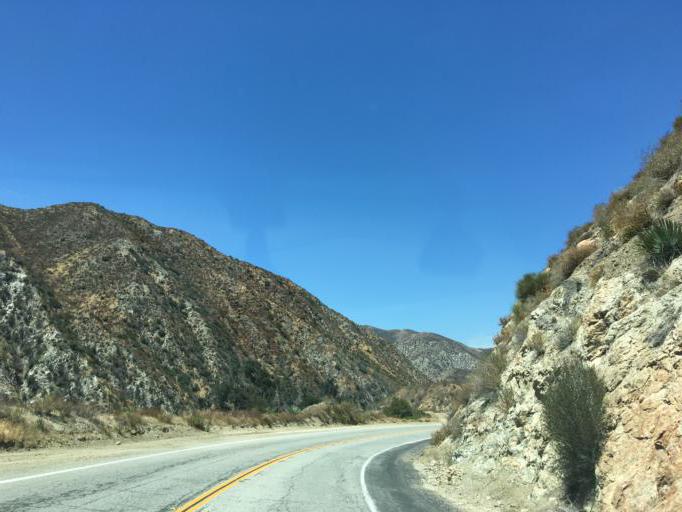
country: US
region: California
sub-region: Los Angeles County
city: La Crescenta-Montrose
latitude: 34.2978
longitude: -118.2467
